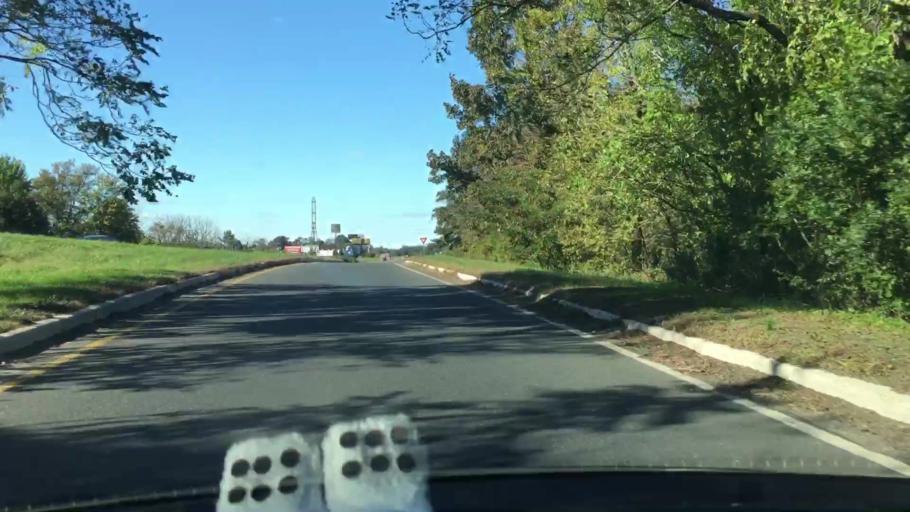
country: US
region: New Jersey
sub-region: Camden County
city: Blackwood
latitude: 39.8038
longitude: -75.0557
